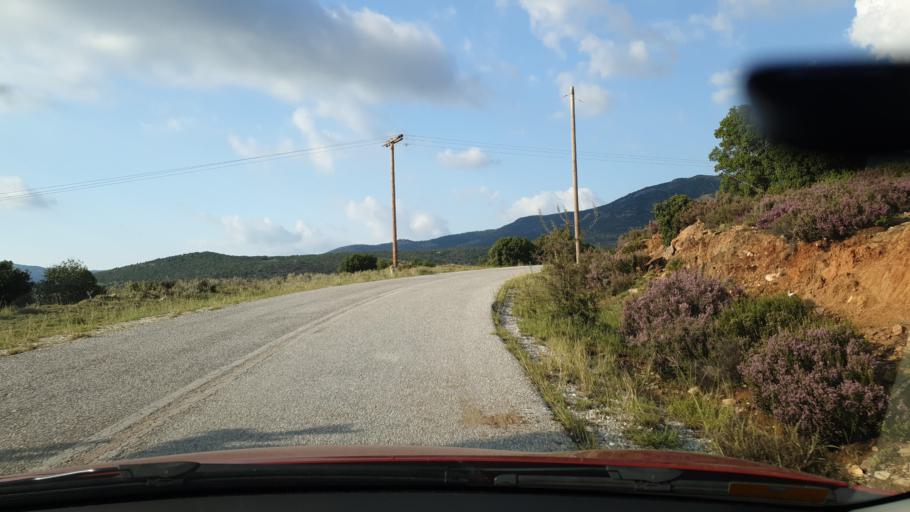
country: GR
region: Central Macedonia
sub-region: Nomos Thessalonikis
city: Peristera
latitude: 40.5145
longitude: 23.1728
